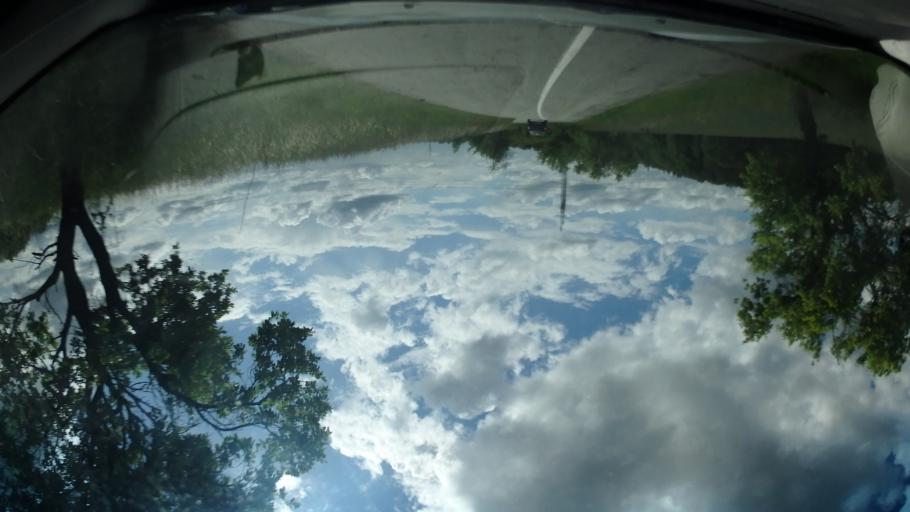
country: CZ
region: South Moravian
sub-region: Okres Blansko
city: Letovice
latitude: 49.6030
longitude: 16.6071
